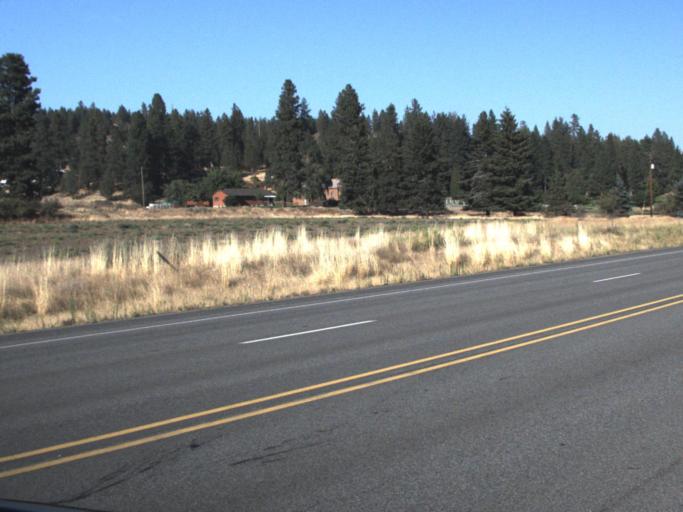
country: US
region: Washington
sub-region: Spokane County
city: Trentwood
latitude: 47.6973
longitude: -117.1681
